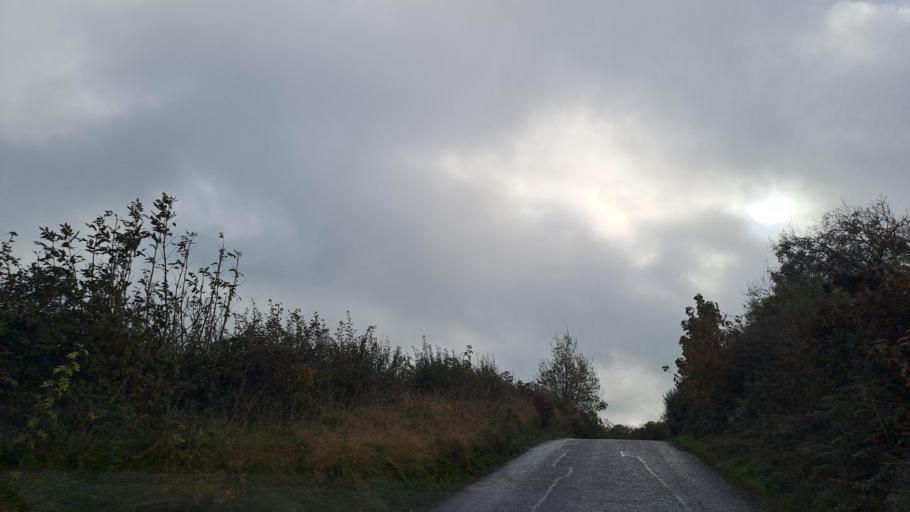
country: IE
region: Ulster
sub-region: An Cabhan
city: Bailieborough
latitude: 53.9743
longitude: -6.9916
